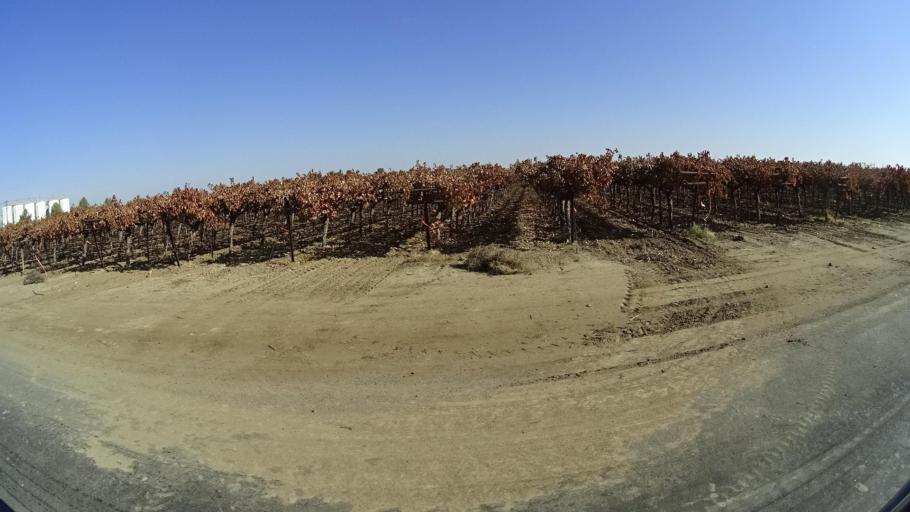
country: US
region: California
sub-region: Kern County
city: McFarland
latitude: 35.7022
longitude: -119.2321
